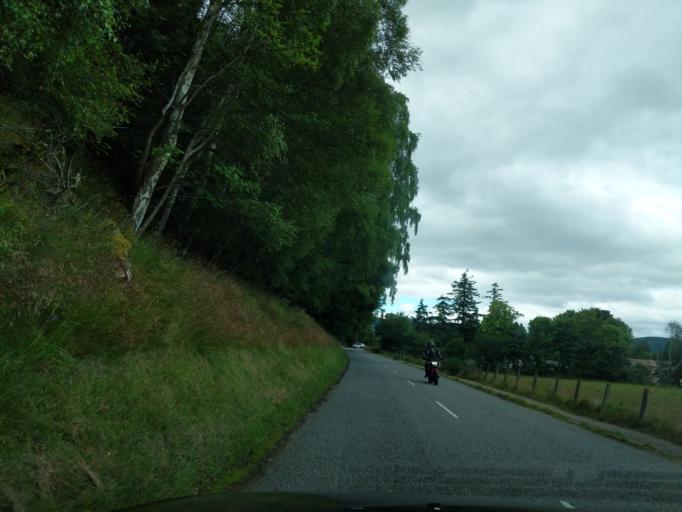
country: GB
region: Scotland
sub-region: Aberdeenshire
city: Ballater
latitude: 57.0478
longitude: -3.0332
